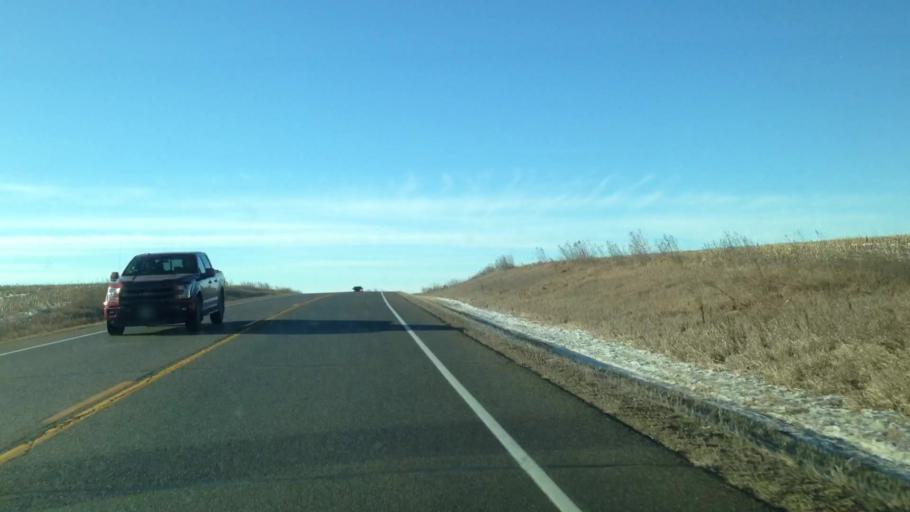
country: US
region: Minnesota
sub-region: Dakota County
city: Farmington
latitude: 44.5622
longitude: -93.0390
